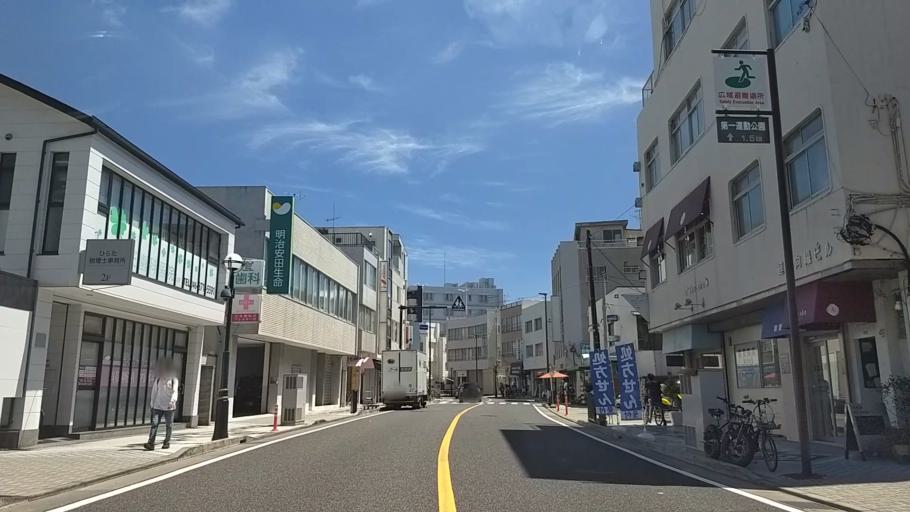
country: JP
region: Kanagawa
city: Zushi
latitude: 35.2957
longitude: 139.5765
